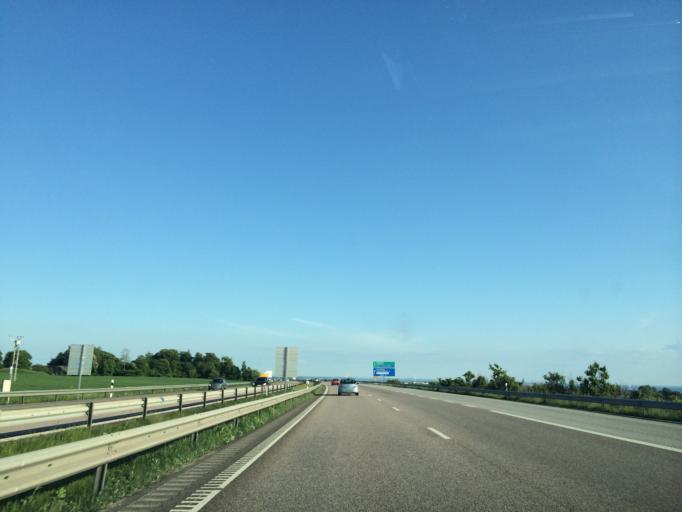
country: SE
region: Skane
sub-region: Helsingborg
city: Glumslov
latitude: 55.9364
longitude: 12.8202
